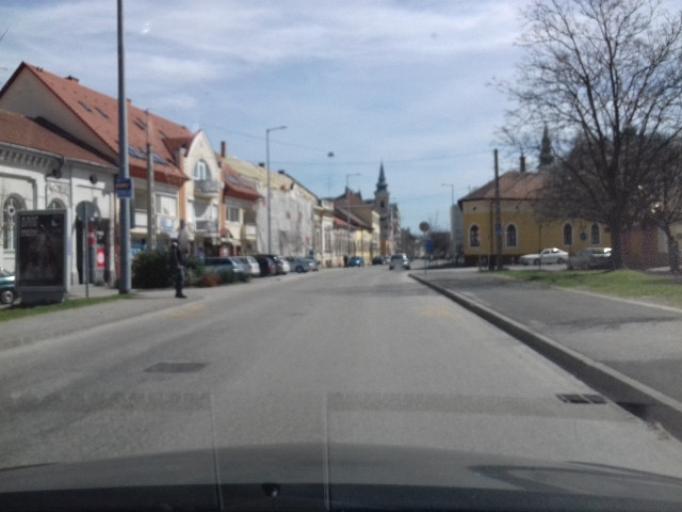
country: HU
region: Bacs-Kiskun
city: Kecskemet
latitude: 46.9099
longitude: 19.6884
